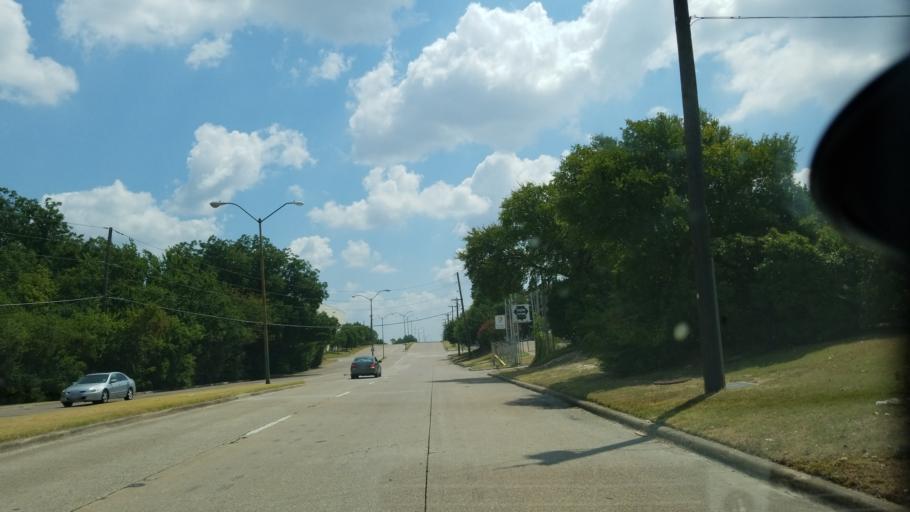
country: US
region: Texas
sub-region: Dallas County
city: Duncanville
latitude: 32.6911
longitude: -96.9005
